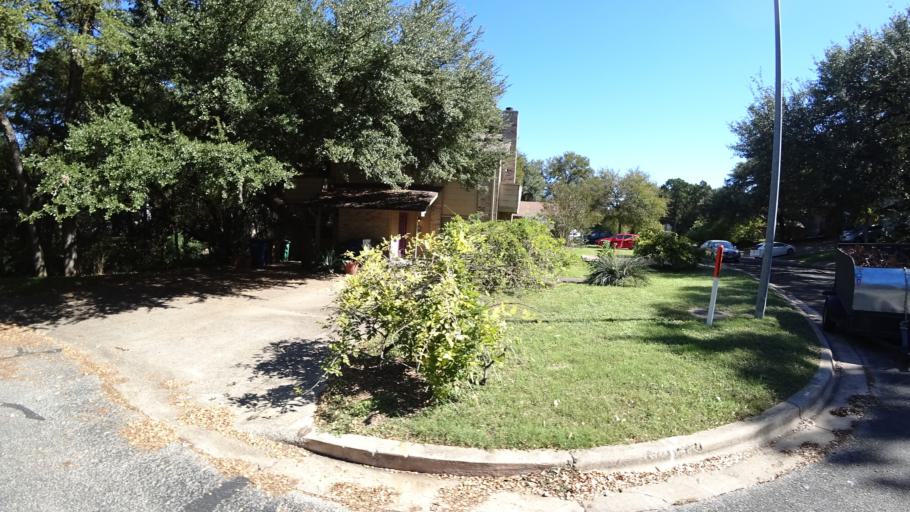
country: US
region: Texas
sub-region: Travis County
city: Rollingwood
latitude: 30.2411
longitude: -97.7763
